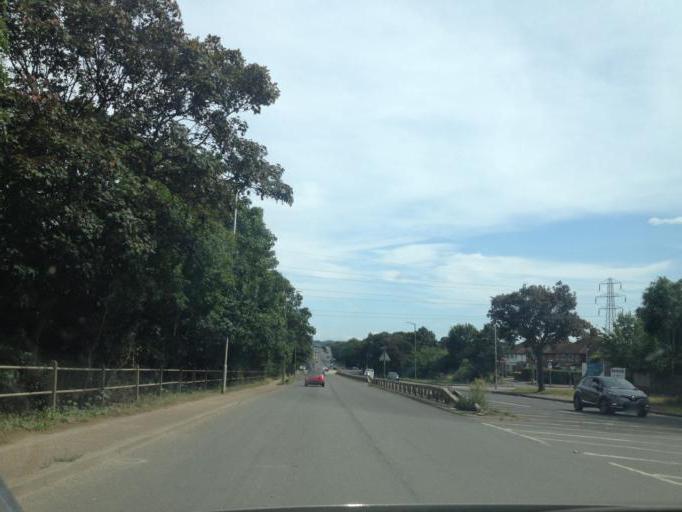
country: GB
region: England
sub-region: Hertfordshire
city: Watford
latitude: 51.6785
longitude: -0.3822
